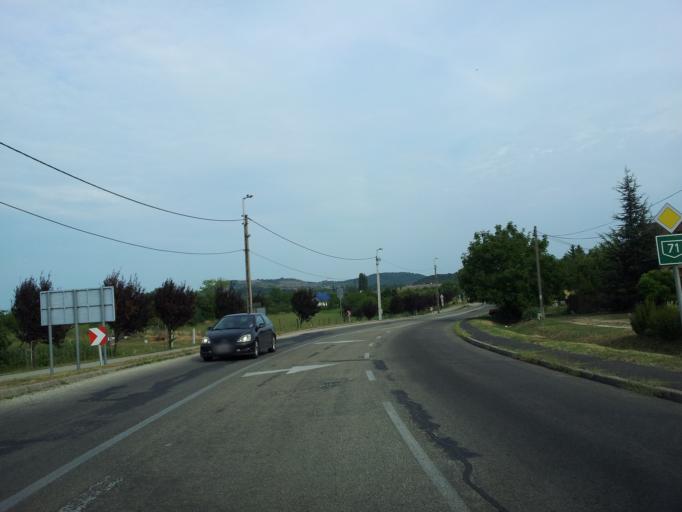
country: HU
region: Veszprem
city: Balatonfured
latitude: 46.9277
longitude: 17.8348
